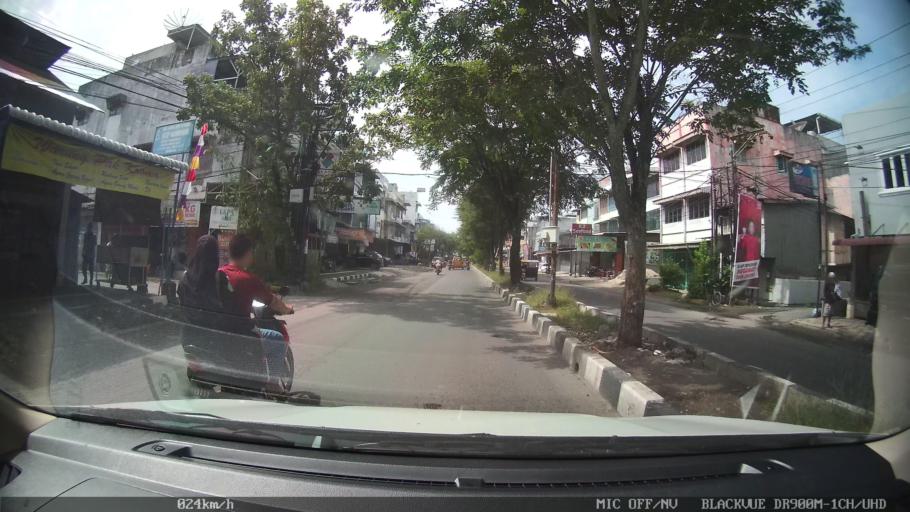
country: ID
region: North Sumatra
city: Medan
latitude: 3.5916
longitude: 98.7062
